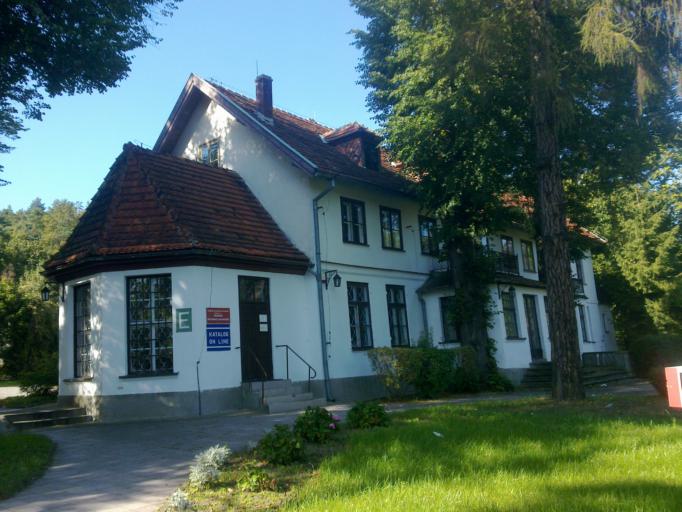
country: PL
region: Pomeranian Voivodeship
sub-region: Sopot
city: Sopot
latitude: 54.4195
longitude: 18.5598
